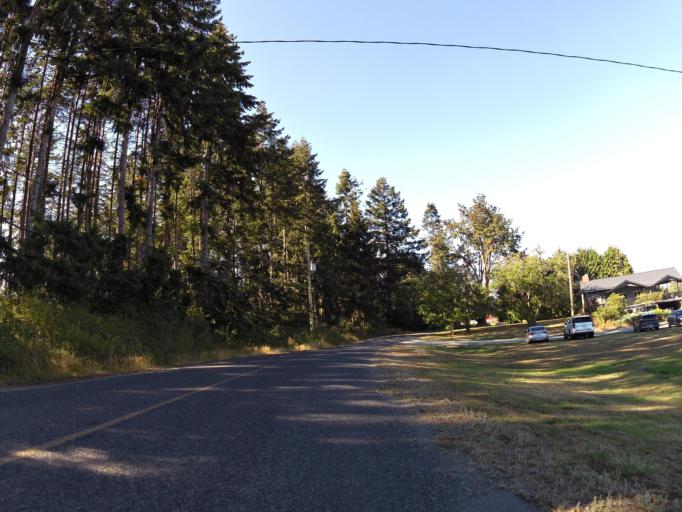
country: CA
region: British Columbia
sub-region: Cowichan Valley Regional District
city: Ladysmith
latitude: 49.0805
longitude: -123.8433
